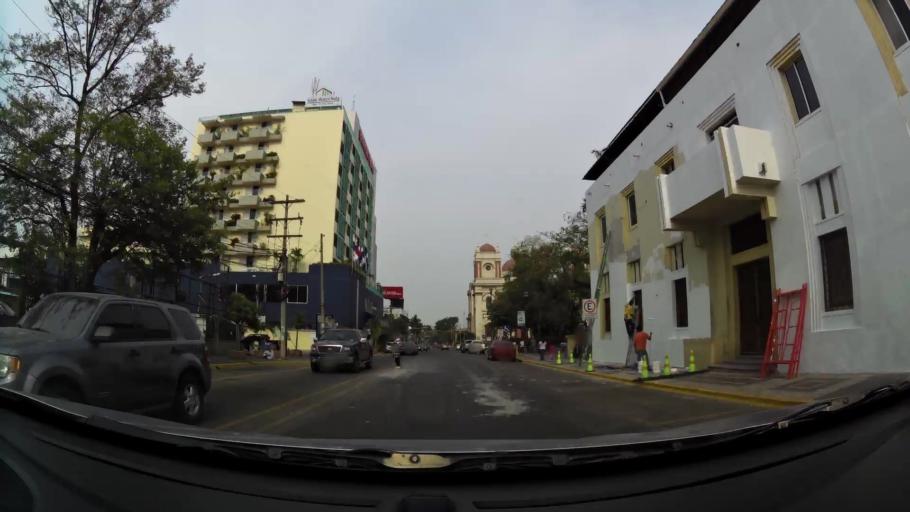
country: HN
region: Cortes
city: San Pedro Sula
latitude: 15.5059
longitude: -88.0257
